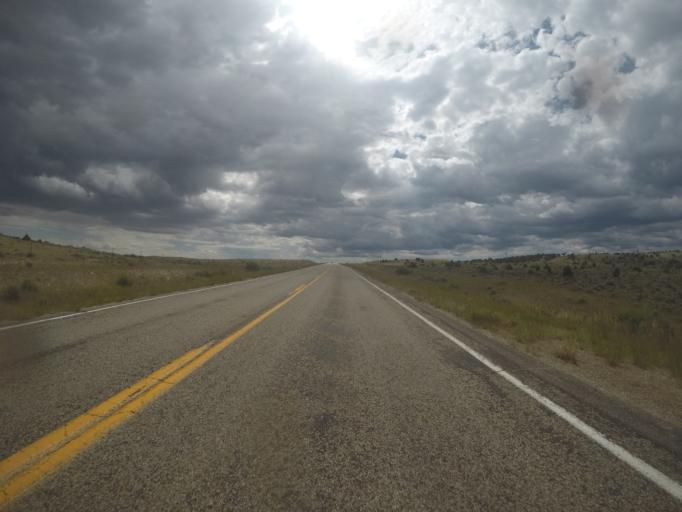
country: US
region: Utah
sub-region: Daggett County
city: Manila
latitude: 41.0207
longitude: -109.8614
